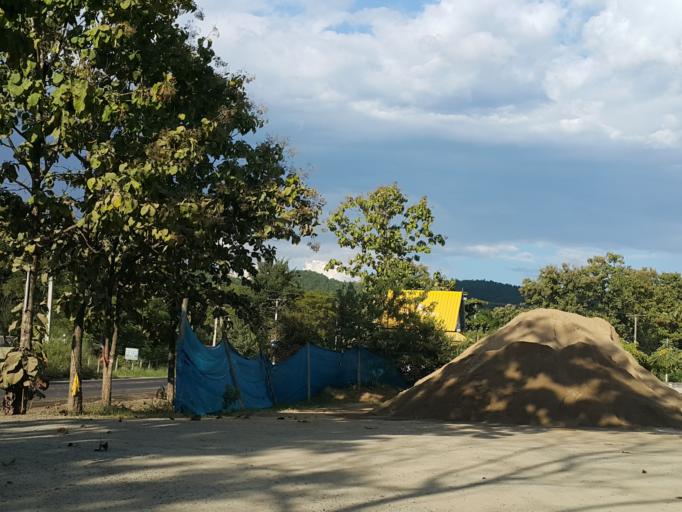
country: TH
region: Chiang Mai
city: Mae On
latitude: 18.8118
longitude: 99.2516
